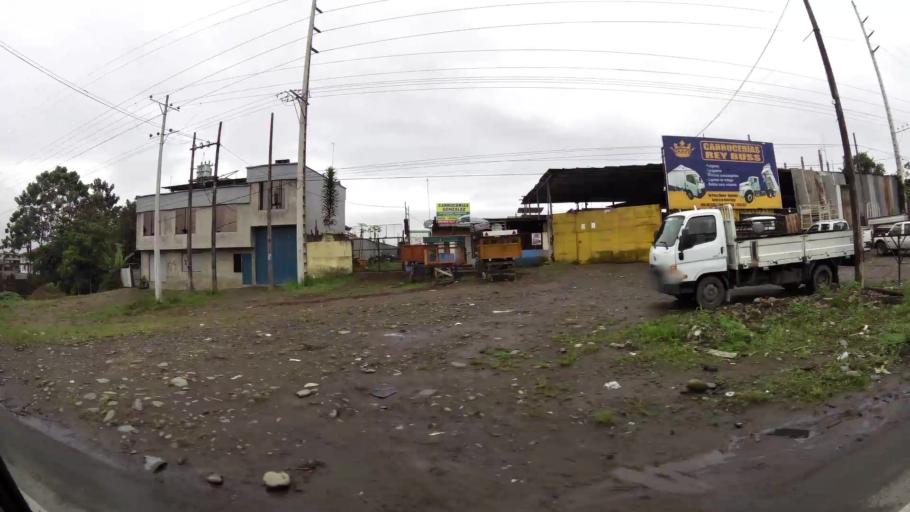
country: EC
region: Santo Domingo de los Tsachilas
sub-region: Canton Santo Domingo de los Colorados
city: Santo Domingo de los Colorados
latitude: -0.2592
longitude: -79.2027
